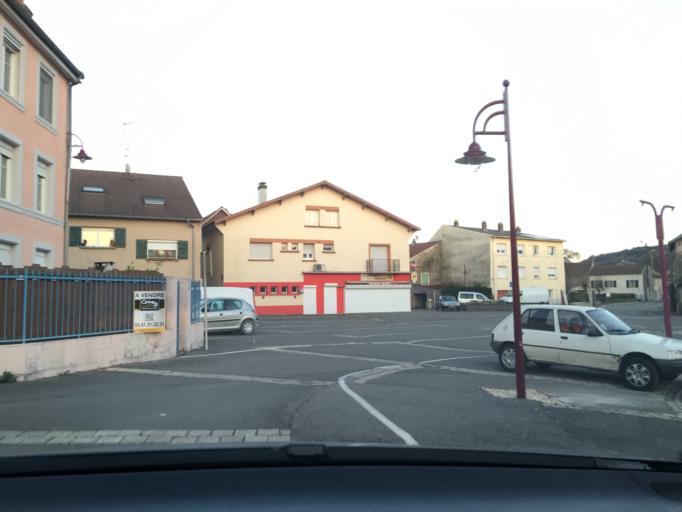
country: FR
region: Franche-Comte
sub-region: Departement du Doubs
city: Bavans
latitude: 47.4808
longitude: 6.7306
